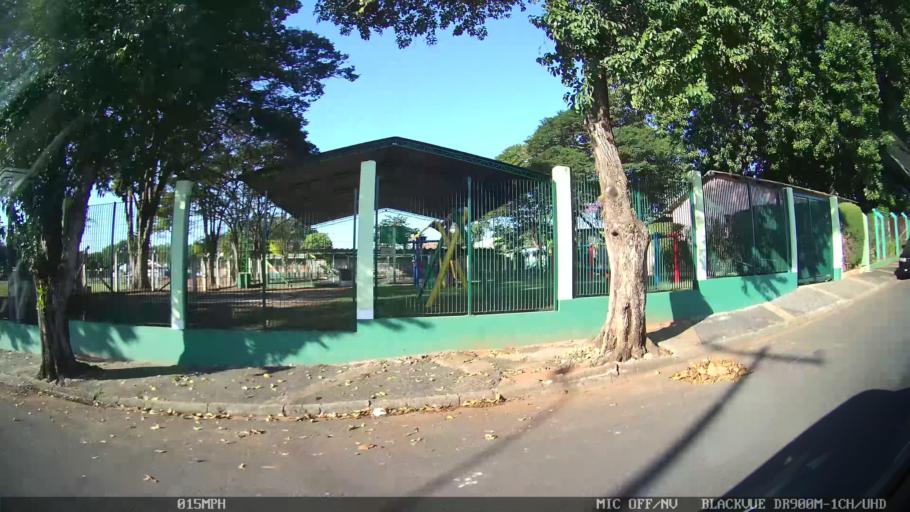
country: BR
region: Sao Paulo
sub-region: Nova Odessa
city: Nova Odessa
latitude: -22.7691
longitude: -47.2932
